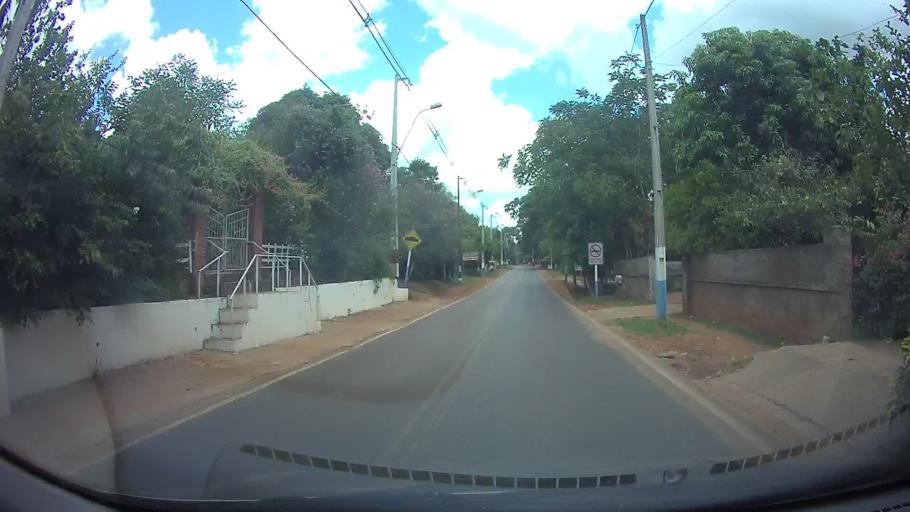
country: PY
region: Central
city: Aregua
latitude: -25.2963
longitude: -57.4410
